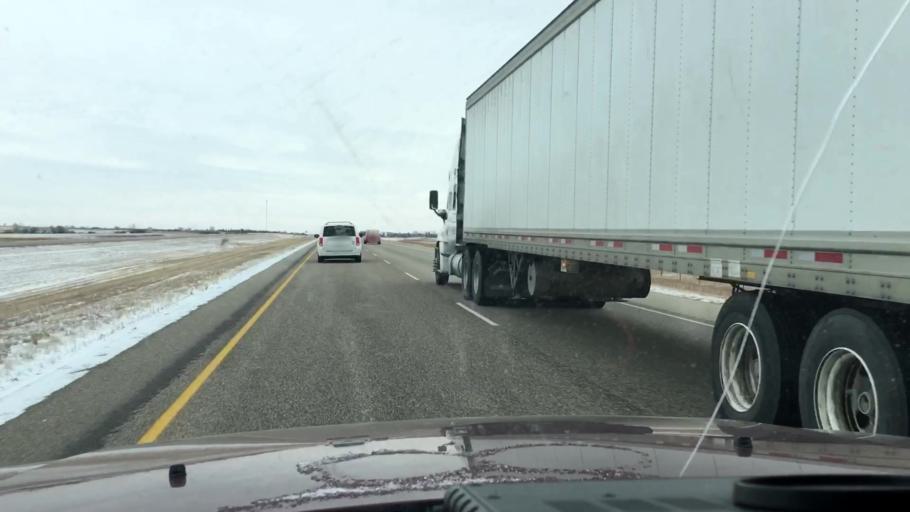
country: CA
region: Saskatchewan
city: Saskatoon
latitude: 51.5179
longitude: -106.2897
